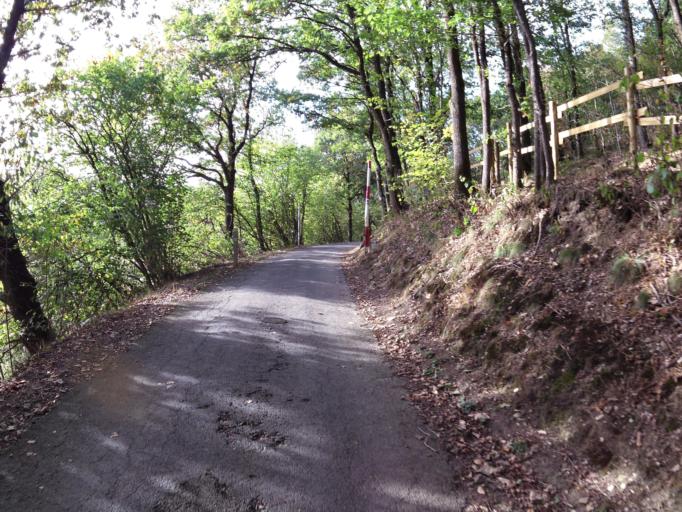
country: BE
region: Wallonia
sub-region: Province de Liege
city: Saint-Vith
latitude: 50.2677
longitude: 6.1392
